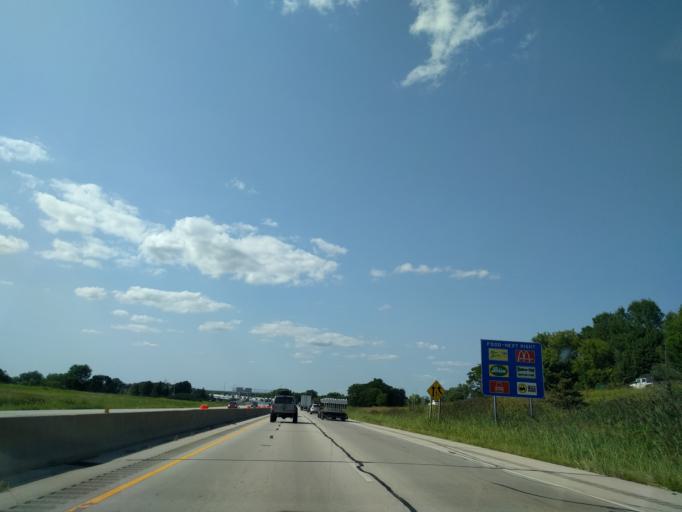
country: US
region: Wisconsin
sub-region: Brown County
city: Allouez
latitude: 44.4710
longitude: -88.0320
